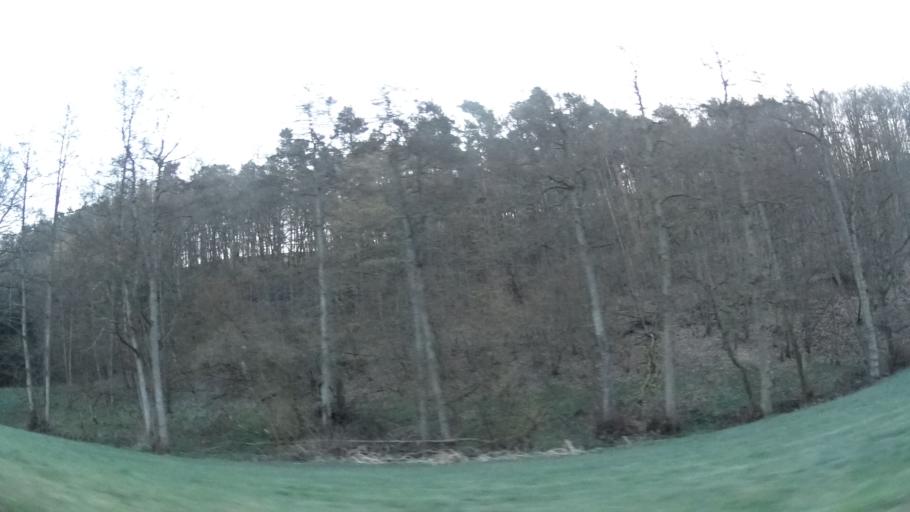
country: DE
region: Rheinland-Pfalz
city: Kirrweiler
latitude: 49.6250
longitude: 7.5051
